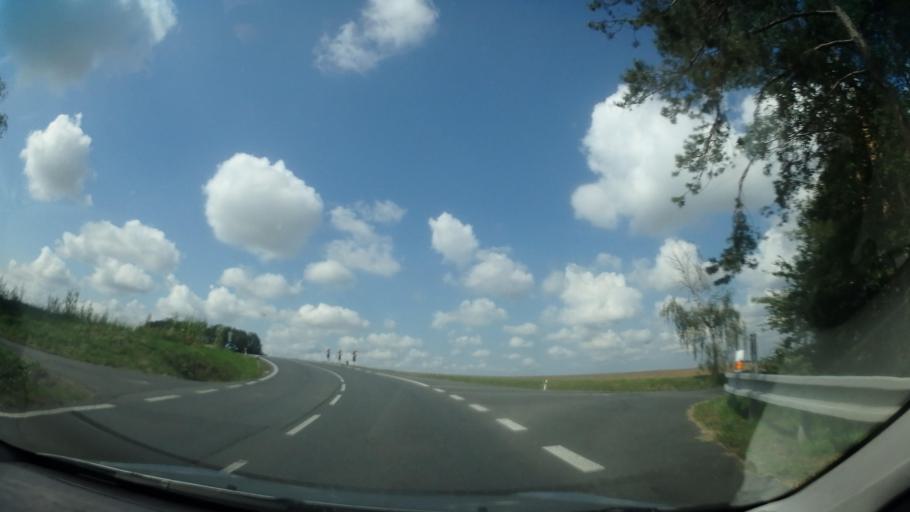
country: CZ
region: Central Bohemia
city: Suchdol
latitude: 49.9561
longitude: 15.1234
